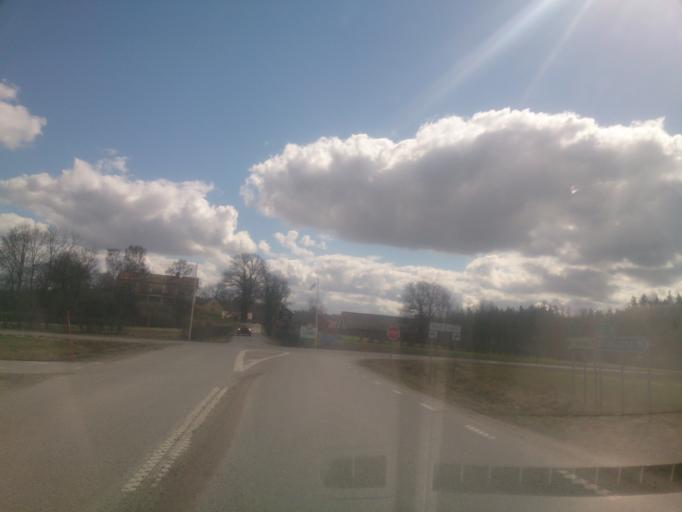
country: SE
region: OEstergoetland
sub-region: Norrkopings Kommun
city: Norrkoping
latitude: 58.5657
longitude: 16.0803
